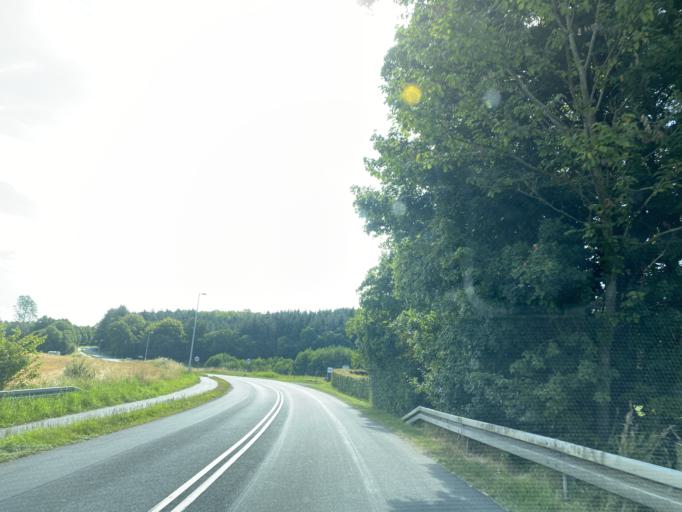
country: DK
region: Central Jutland
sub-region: Favrskov Kommune
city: Hammel
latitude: 56.2651
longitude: 9.8369
